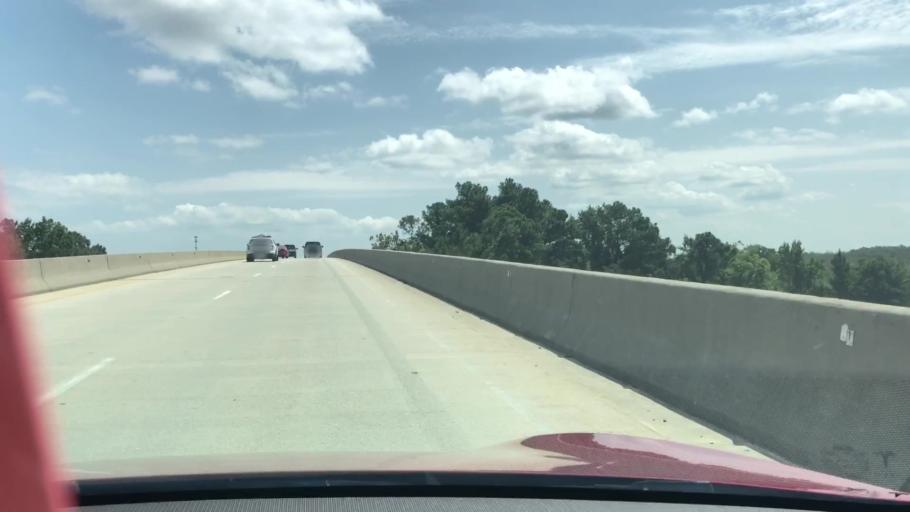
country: US
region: North Carolina
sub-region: Currituck County
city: Currituck
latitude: 36.3420
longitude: -75.9559
